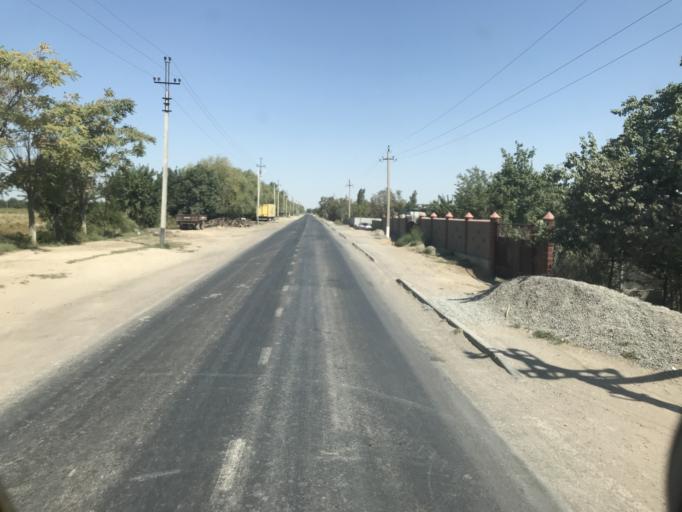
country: KZ
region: Ongtustik Qazaqstan
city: Ilyich
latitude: 40.9377
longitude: 68.4883
